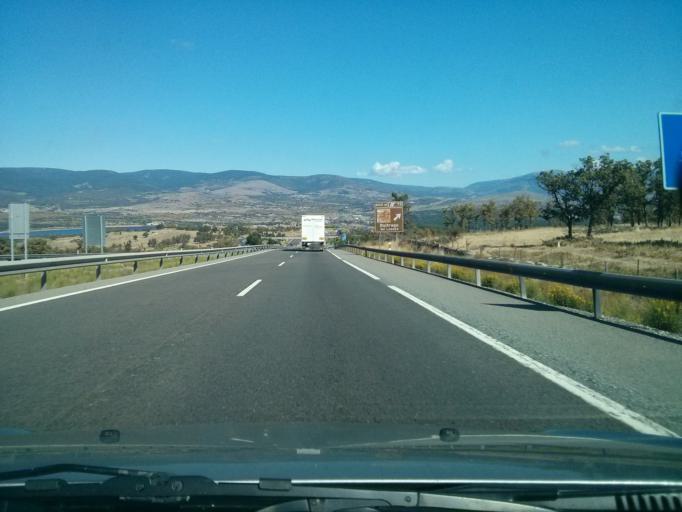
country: ES
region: Madrid
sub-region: Provincia de Madrid
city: Buitrago del Lozoya
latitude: 40.9588
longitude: -3.6415
